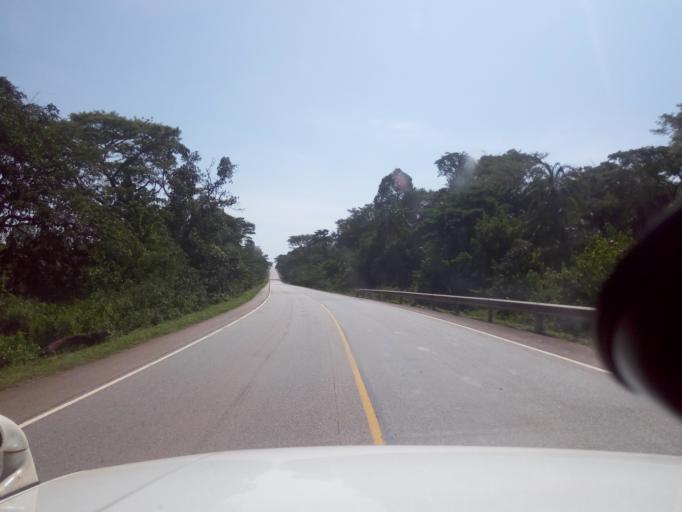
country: UG
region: Eastern Region
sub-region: Busia District
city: Busia
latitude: 0.5390
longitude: 34.0076
